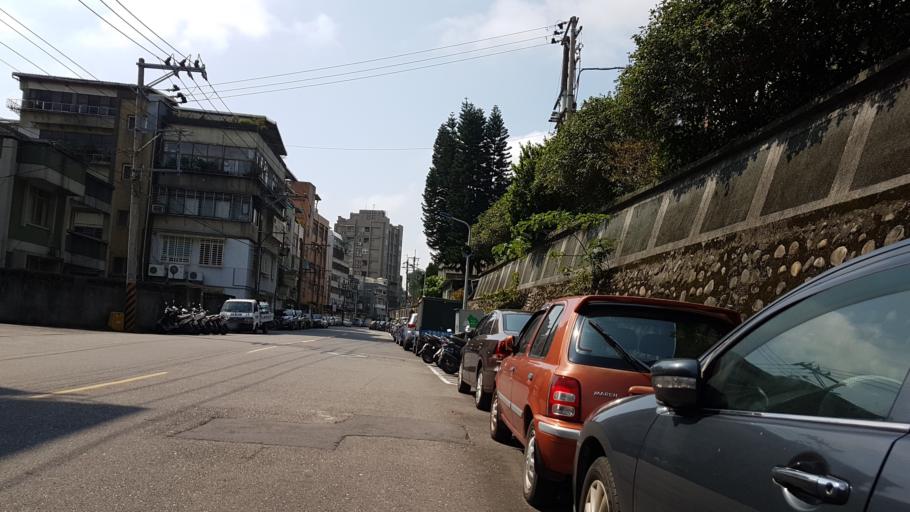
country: TW
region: Taipei
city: Taipei
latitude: 25.0065
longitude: 121.5403
